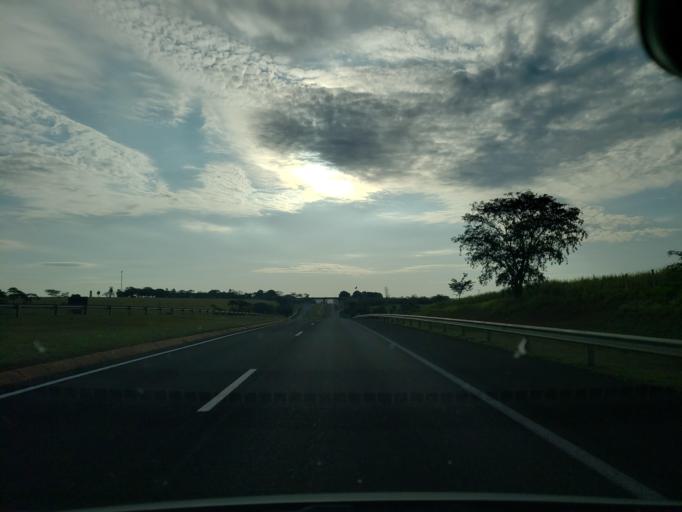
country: BR
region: Sao Paulo
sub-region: Mirandopolis
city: Mirandopolis
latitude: -21.0901
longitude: -51.0566
